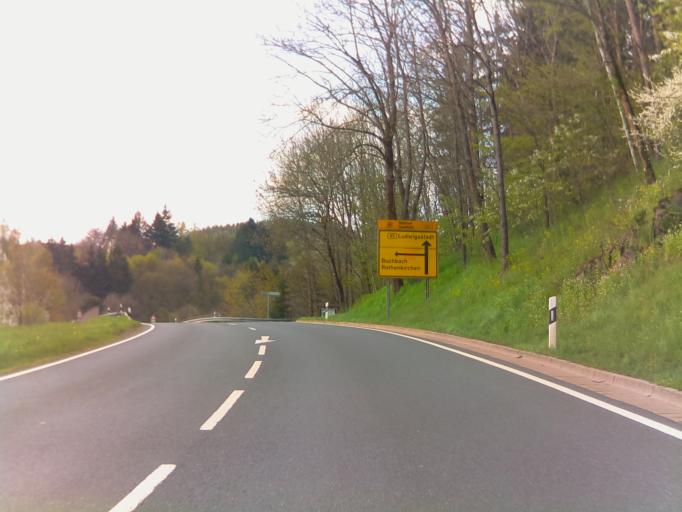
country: DE
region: Bavaria
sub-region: Upper Franconia
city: Pressig
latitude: 50.3633
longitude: 11.3220
